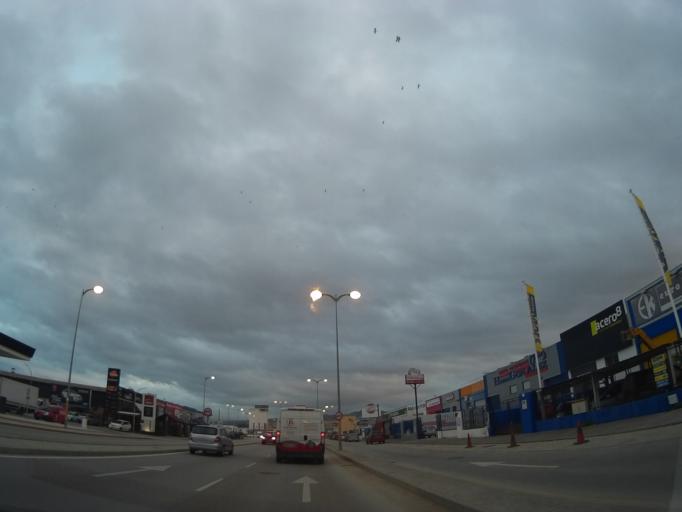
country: ES
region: Andalusia
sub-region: Provincia de Malaga
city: Alhaurin de la Torre
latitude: 36.6952
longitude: -4.4938
